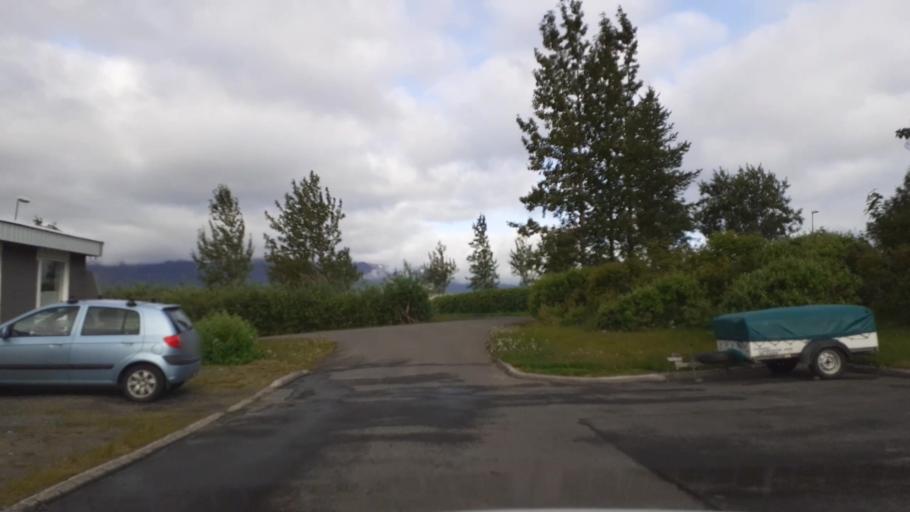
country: IS
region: Northeast
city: Akureyri
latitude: 65.7480
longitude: -18.0816
